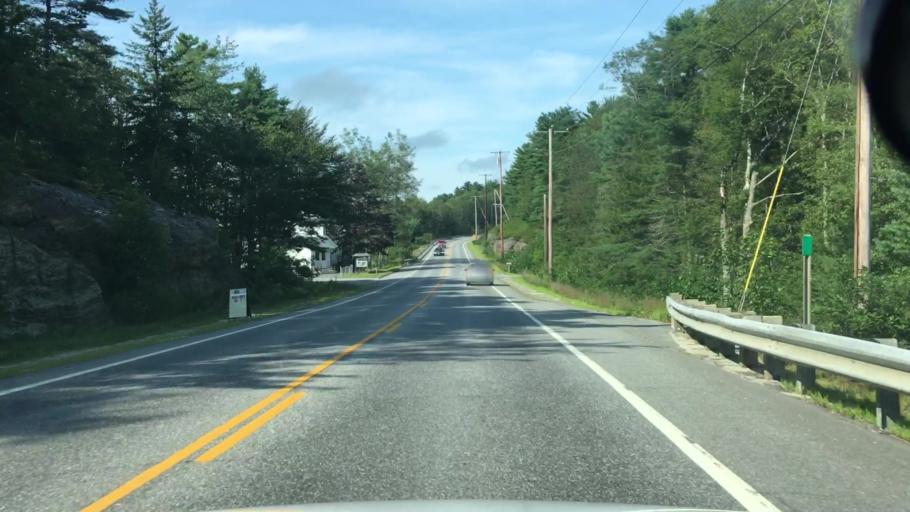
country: US
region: Maine
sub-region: Cumberland County
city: Harpswell Center
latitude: 43.8054
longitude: -69.9321
